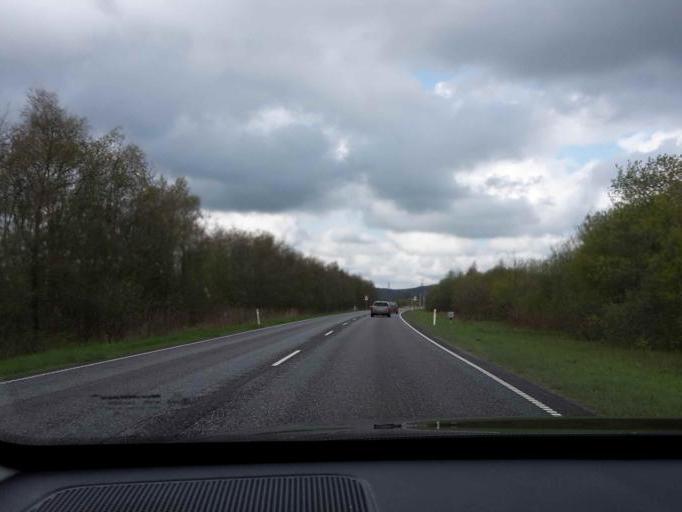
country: DK
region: South Denmark
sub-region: Vejle Kommune
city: Vejle
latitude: 55.7045
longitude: 9.5053
